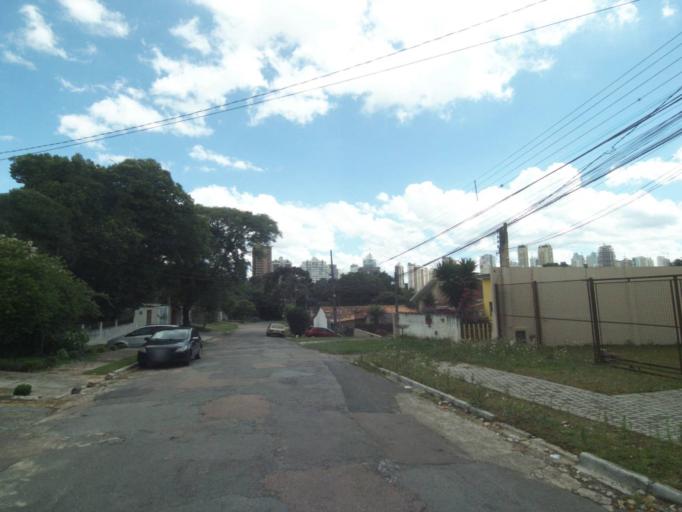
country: BR
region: Parana
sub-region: Curitiba
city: Curitiba
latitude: -25.4317
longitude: -49.3289
